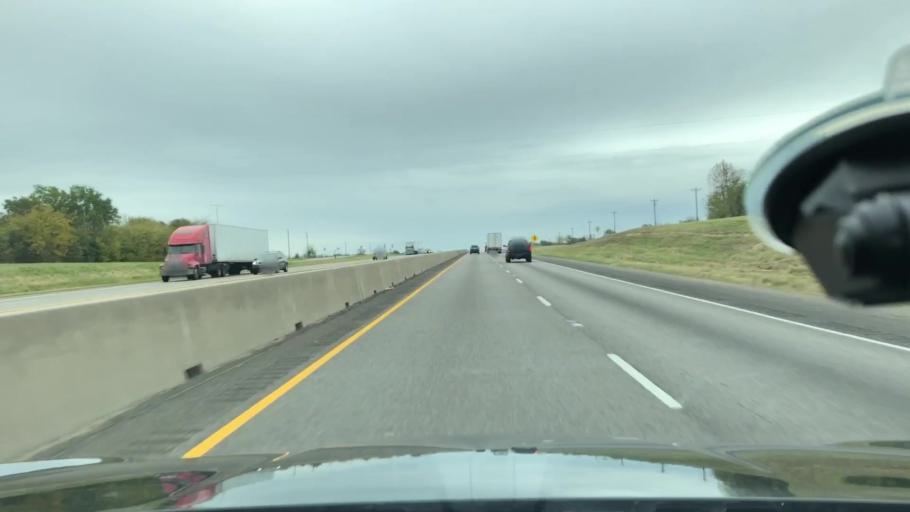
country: US
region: Texas
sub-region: Hopkins County
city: Sulphur Springs
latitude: 33.1467
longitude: -95.4937
